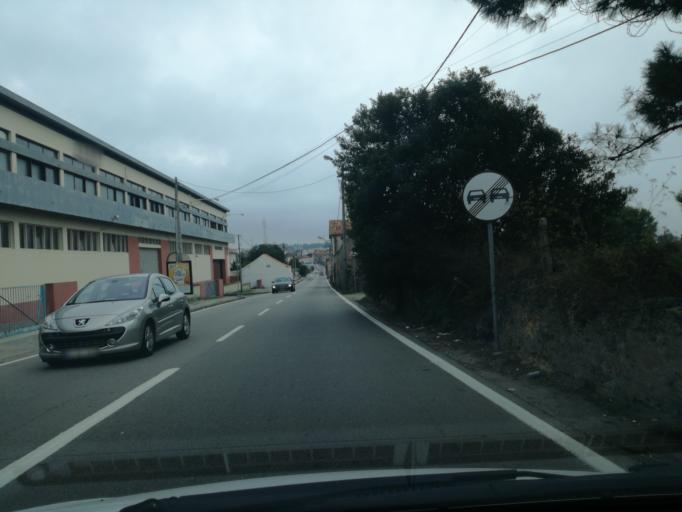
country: PT
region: Aveiro
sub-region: Espinho
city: Espinho
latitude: 41.0002
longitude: -8.6378
